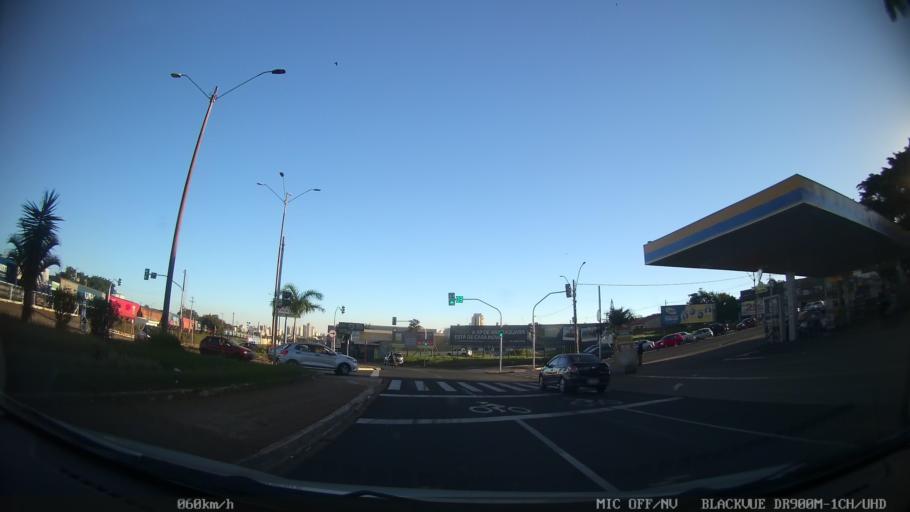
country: BR
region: Sao Paulo
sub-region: Araraquara
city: Araraquara
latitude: -21.7786
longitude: -48.1694
